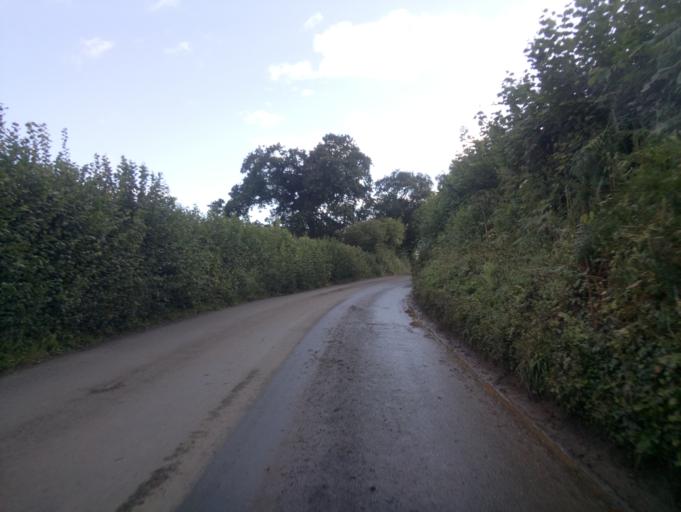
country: GB
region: England
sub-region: Devon
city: Ivybridge
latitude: 50.3660
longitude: -3.9112
